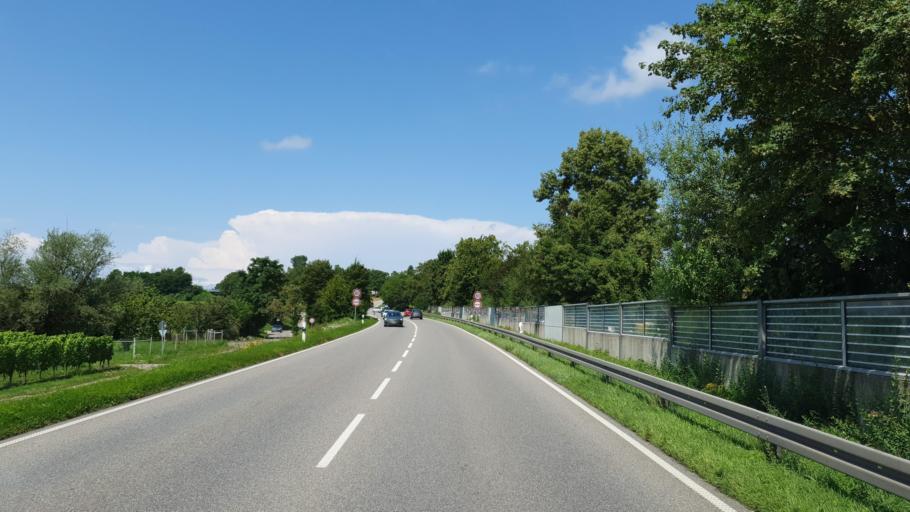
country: DE
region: Baden-Wuerttemberg
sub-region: Tuebingen Region
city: Stetten
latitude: 47.6874
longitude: 9.3009
